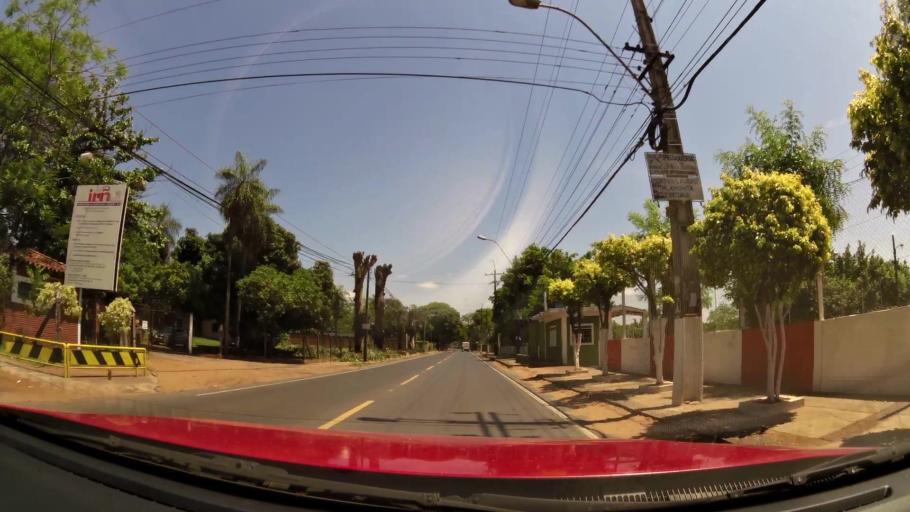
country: PY
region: Central
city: Nemby
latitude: -25.3968
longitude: -57.5378
